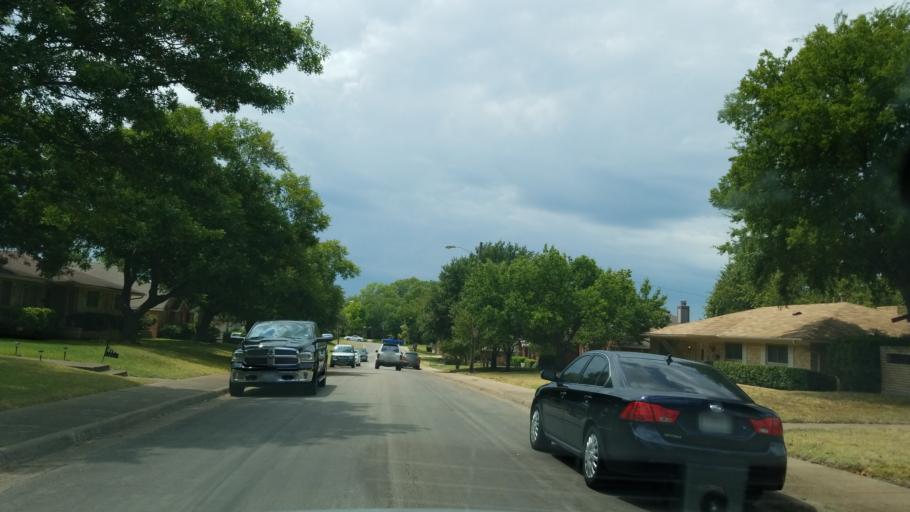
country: US
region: Texas
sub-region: Dallas County
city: Duncanville
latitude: 32.6607
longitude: -96.8518
